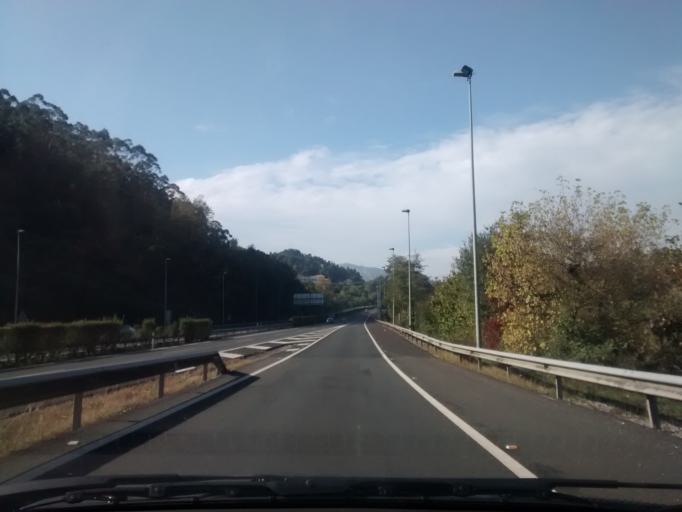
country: ES
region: Cantabria
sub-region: Provincia de Cantabria
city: Entrambasaguas
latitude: 43.3913
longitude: -3.7085
